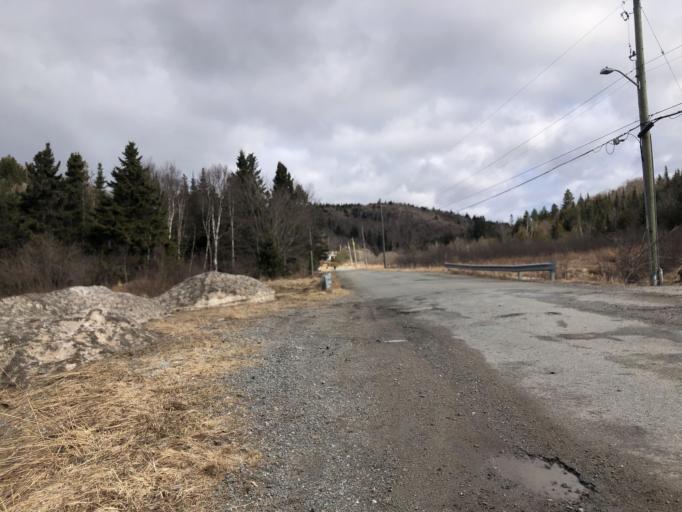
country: CA
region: New Brunswick
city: Saint John
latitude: 45.3254
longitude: -66.0126
